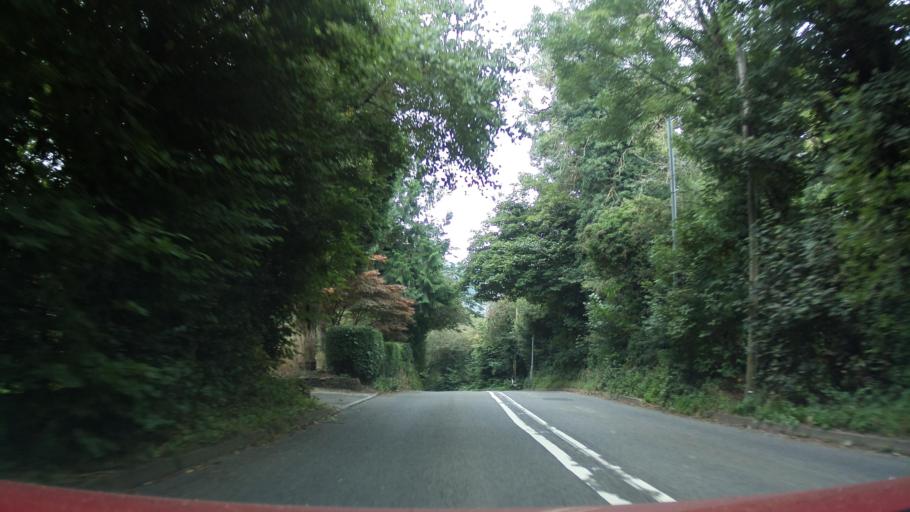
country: GB
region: England
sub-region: Staffordshire
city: Cheadle
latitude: 53.0254
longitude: -1.9575
